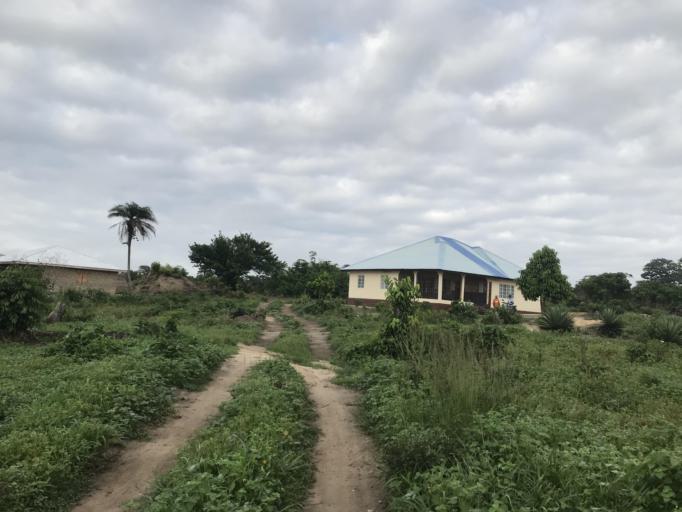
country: SL
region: Eastern Province
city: Pendembu
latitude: 8.0849
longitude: -10.6926
